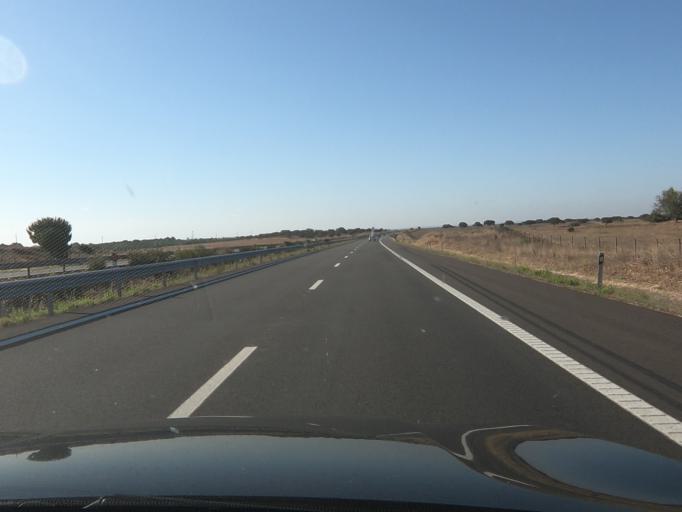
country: PT
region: Beja
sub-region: Aljustrel
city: Aljustrel
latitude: 38.0267
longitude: -8.2878
